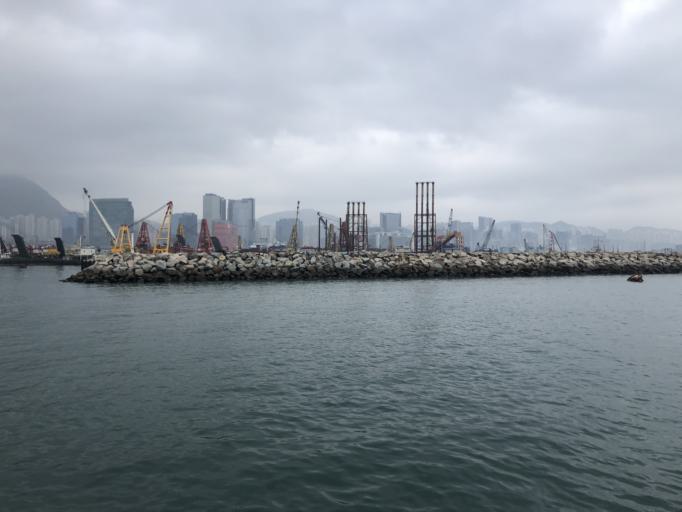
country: HK
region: Kowloon City
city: Kowloon
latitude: 22.3136
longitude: 114.1938
